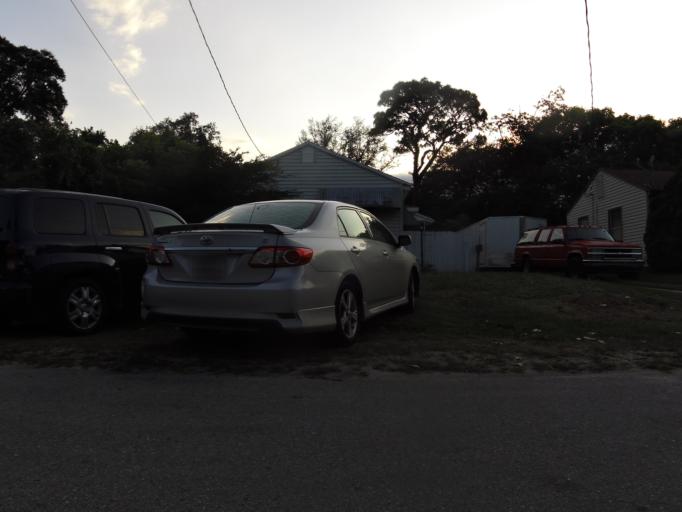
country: US
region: Florida
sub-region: Duval County
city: Jacksonville
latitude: 30.3035
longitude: -81.6242
